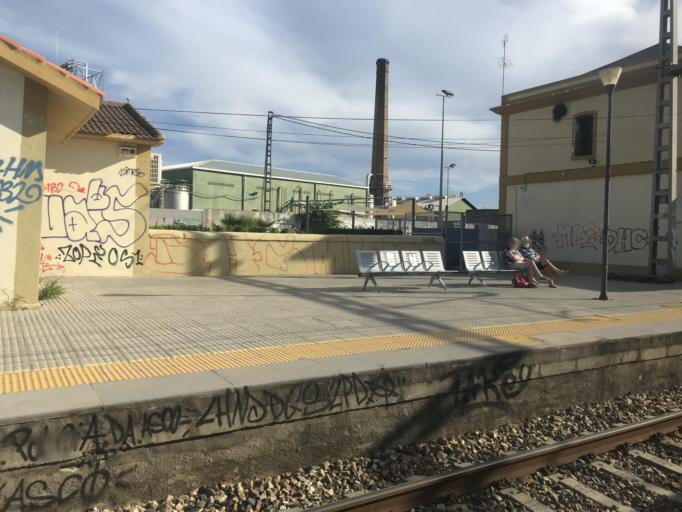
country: ES
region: Valencia
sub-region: Provincia de Castello
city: Benicarlo
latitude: 40.4280
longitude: 0.4153
